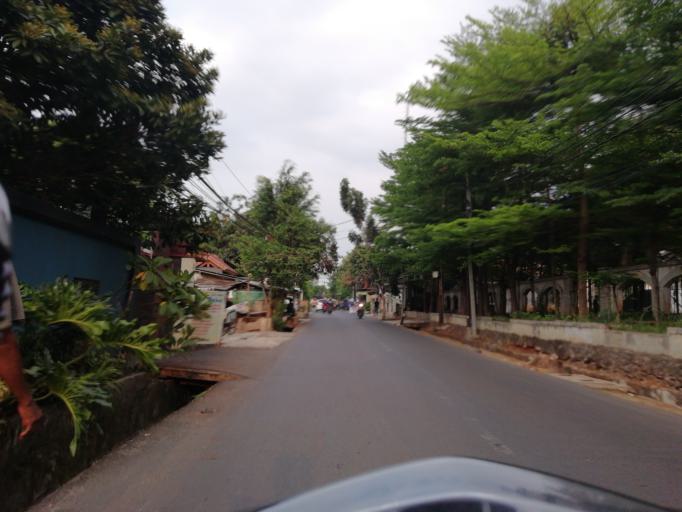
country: ID
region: West Java
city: Depok
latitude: -6.3271
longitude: 106.8130
